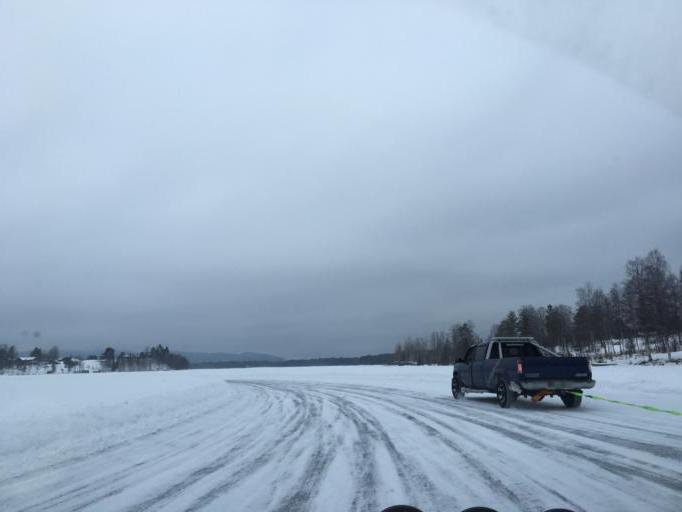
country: SE
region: Dalarna
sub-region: Alvdalens Kommun
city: AElvdalen
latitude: 61.2600
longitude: 14.0906
